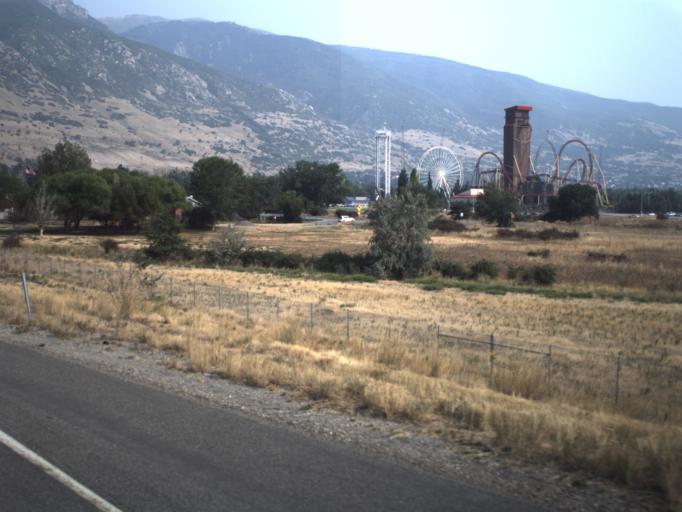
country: US
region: Utah
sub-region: Davis County
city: Farmington
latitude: 40.9913
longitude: -111.9004
